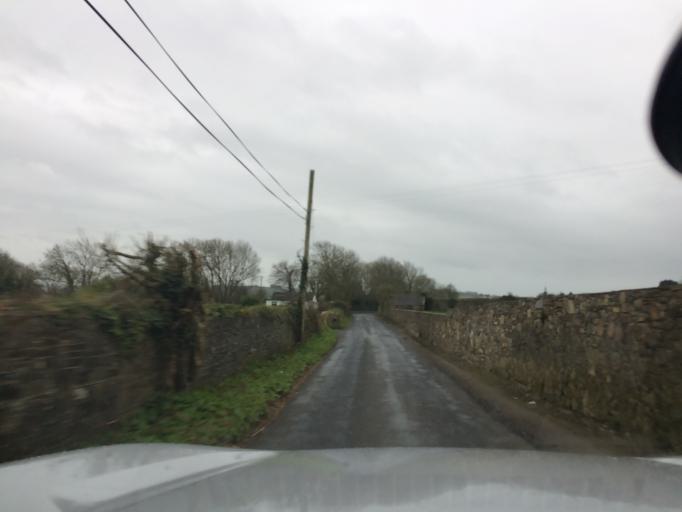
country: IE
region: Munster
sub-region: Waterford
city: Tra Mhor
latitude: 52.2278
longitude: -7.1830
